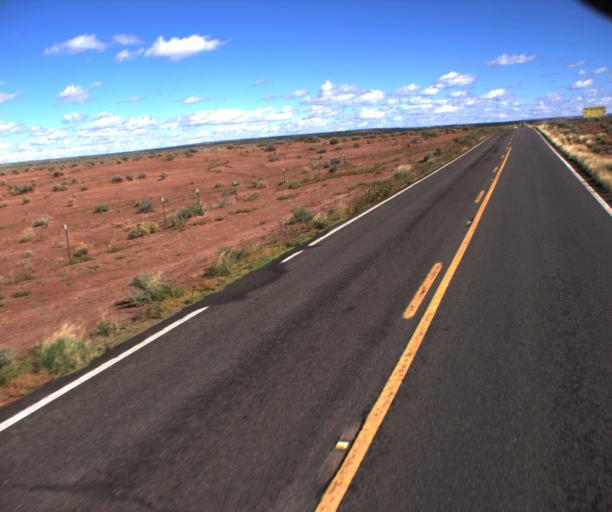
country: US
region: Arizona
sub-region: Apache County
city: Saint Johns
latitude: 34.6955
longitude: -109.2740
